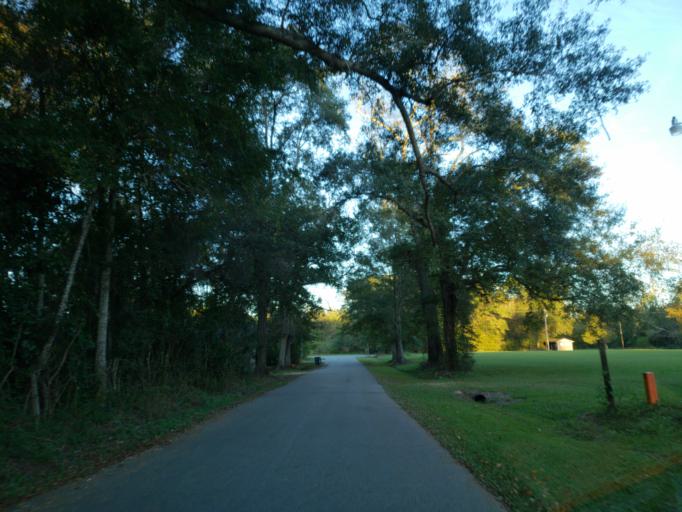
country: US
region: Mississippi
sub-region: Wayne County
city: Belmont
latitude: 31.4330
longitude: -88.4742
